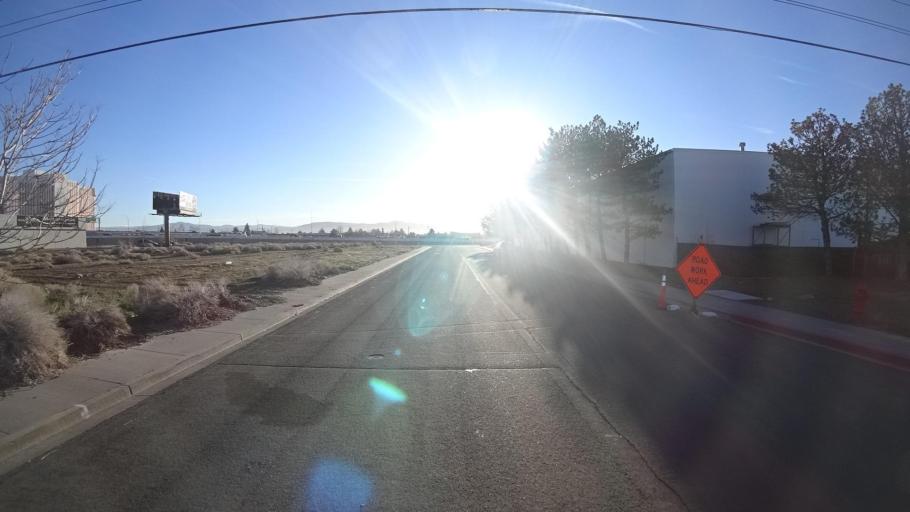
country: US
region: Nevada
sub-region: Washoe County
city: Reno
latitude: 39.5171
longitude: -119.7845
